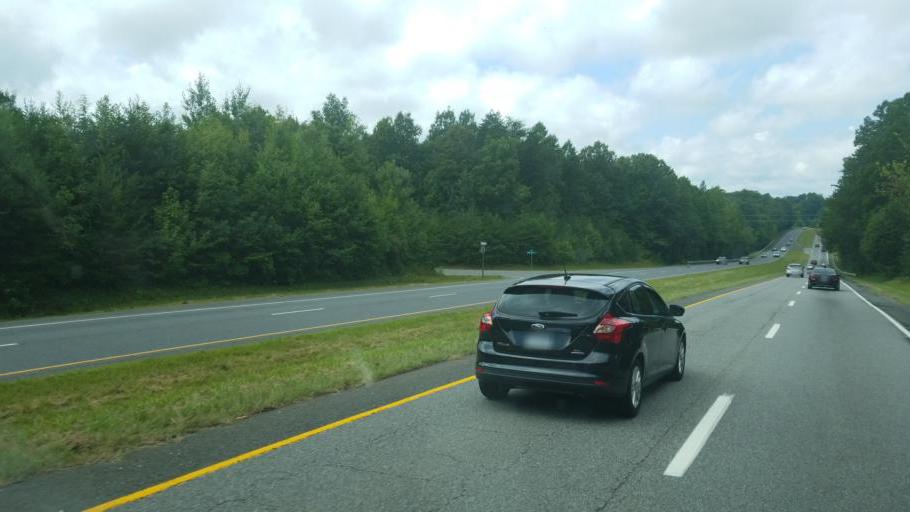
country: US
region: Virginia
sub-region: Stafford County
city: Falmouth
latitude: 38.4079
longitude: -77.5923
